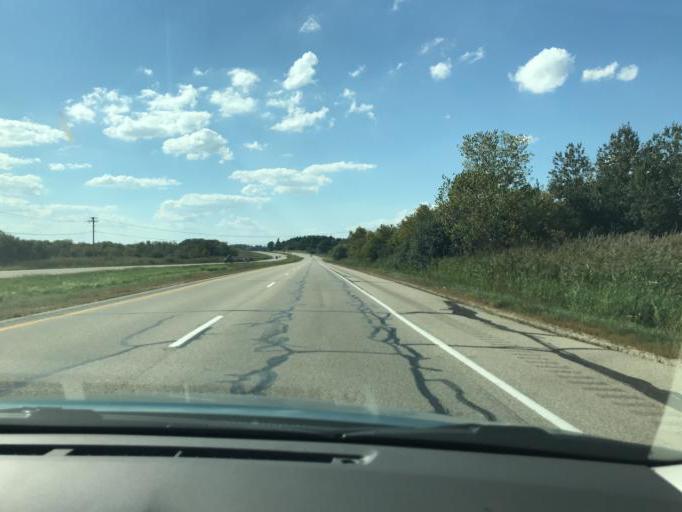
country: US
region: Wisconsin
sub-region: Walworth County
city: Lake Geneva
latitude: 42.5955
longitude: -88.3909
